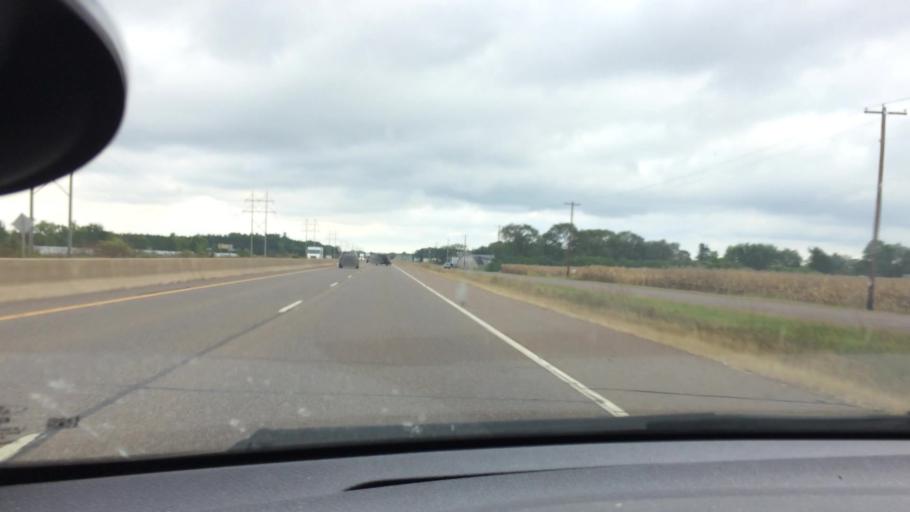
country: US
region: Wisconsin
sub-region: Chippewa County
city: Chippewa Falls
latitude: 44.9024
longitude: -91.4118
